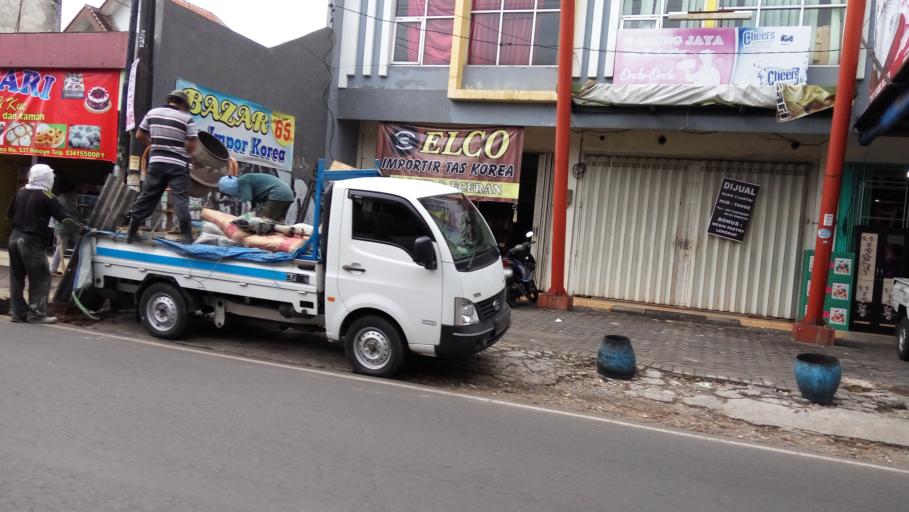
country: ID
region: East Java
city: Malang
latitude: -7.9446
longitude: 112.6098
